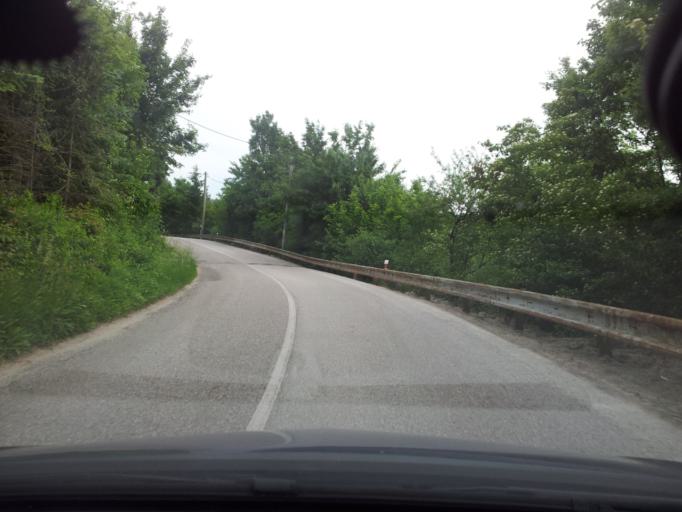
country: SK
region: Nitriansky
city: Partizanske
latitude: 48.5819
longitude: 18.4529
